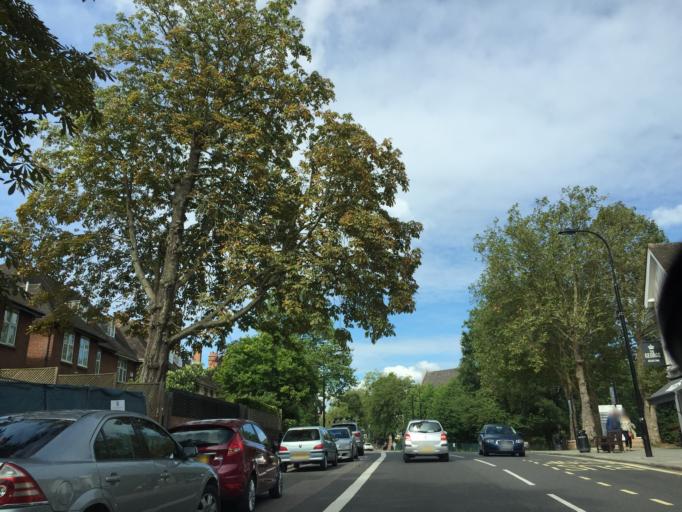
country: GB
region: England
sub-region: Greater London
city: Belsize Park
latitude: 51.5521
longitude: -0.1672
